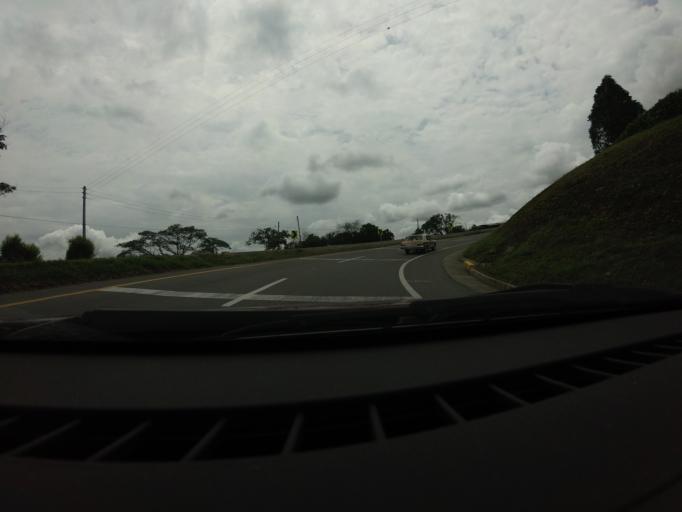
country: CO
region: Cundinamarca
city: La Vega
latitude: 4.9930
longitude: -74.3238
